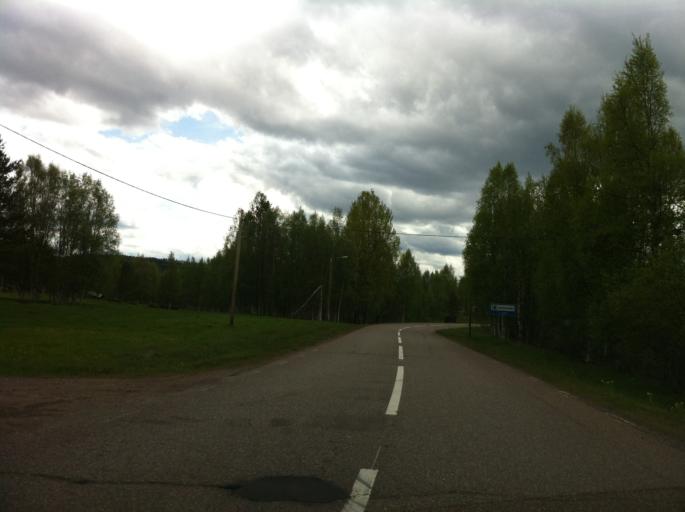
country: NO
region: Hedmark
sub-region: Trysil
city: Innbygda
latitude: 61.4217
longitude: 13.0863
